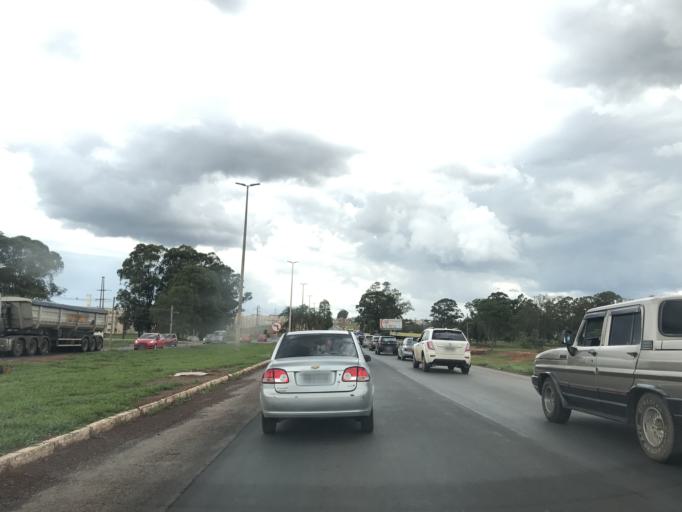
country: BR
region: Federal District
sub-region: Brasilia
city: Brasilia
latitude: -15.8886
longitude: -48.0584
